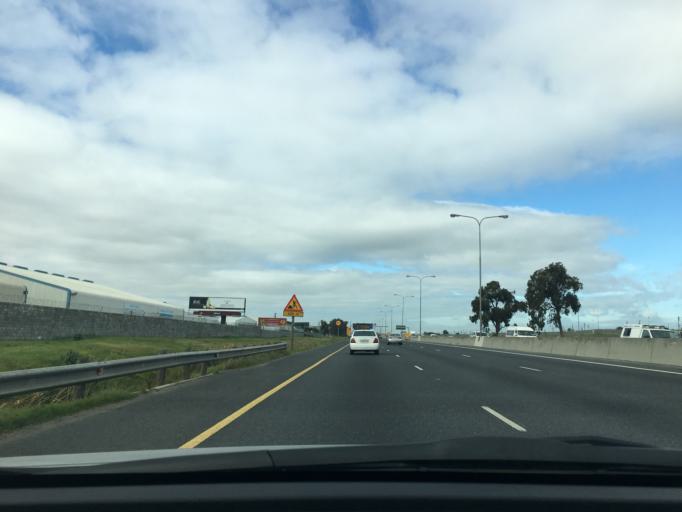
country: ZA
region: Western Cape
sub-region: City of Cape Town
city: Lansdowne
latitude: -33.9719
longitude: 18.5776
